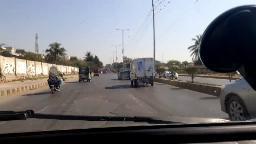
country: PK
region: Sindh
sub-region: Karachi District
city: Karachi
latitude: 24.8958
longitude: 67.0952
